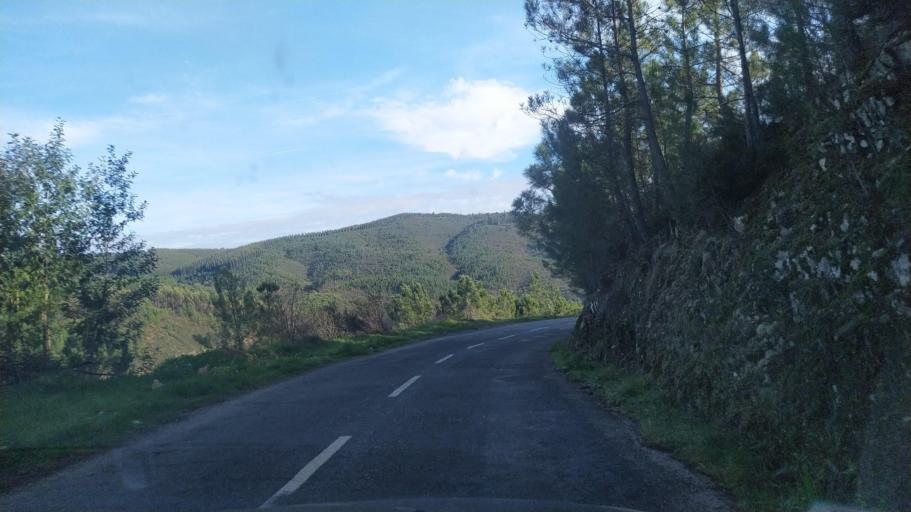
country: PT
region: Castelo Branco
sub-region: Concelho do Fundao
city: Aldeia de Joanes
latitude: 40.1840
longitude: -7.6989
